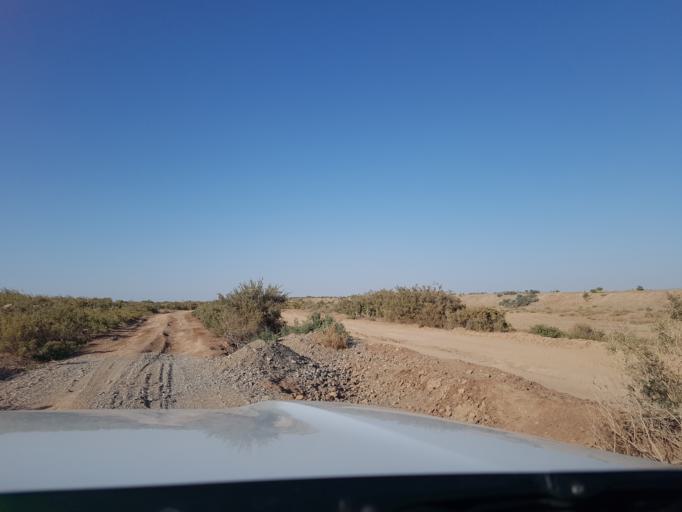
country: IR
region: Razavi Khorasan
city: Sarakhs
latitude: 36.9806
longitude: 61.3857
